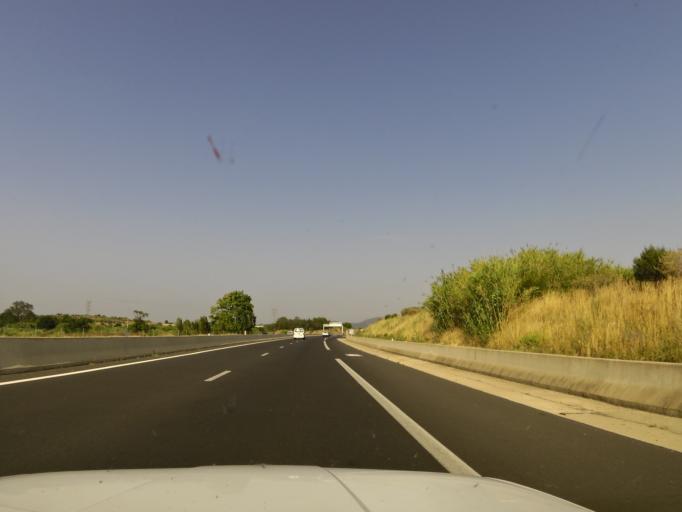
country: FR
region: Languedoc-Roussillon
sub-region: Departement de l'Herault
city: Saint-Andre-de-Sangonis
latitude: 43.6594
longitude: 3.5013
